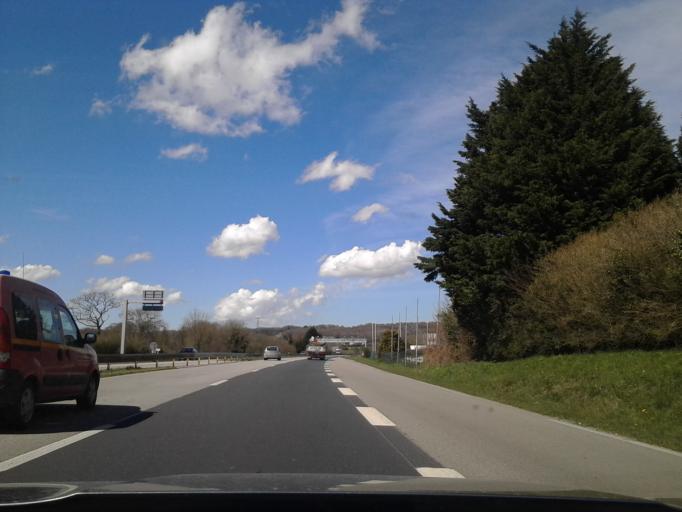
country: FR
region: Lower Normandy
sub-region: Departement de la Manche
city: Brix
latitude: 49.5343
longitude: -1.5329
